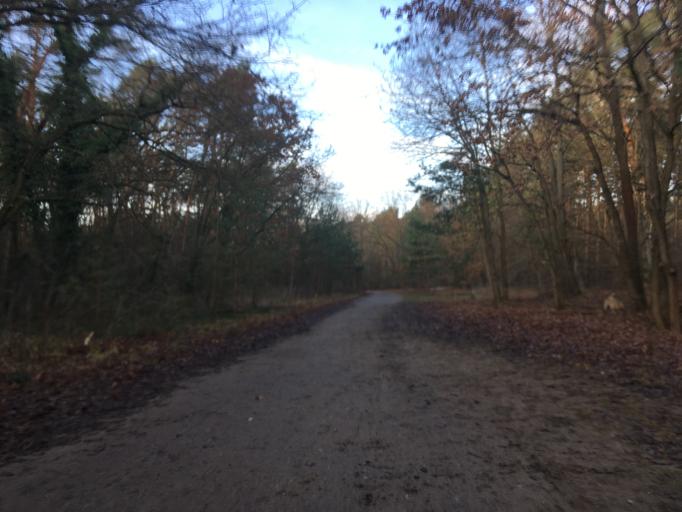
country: DE
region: Berlin
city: Johannisthal
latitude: 52.4504
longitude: 13.4985
